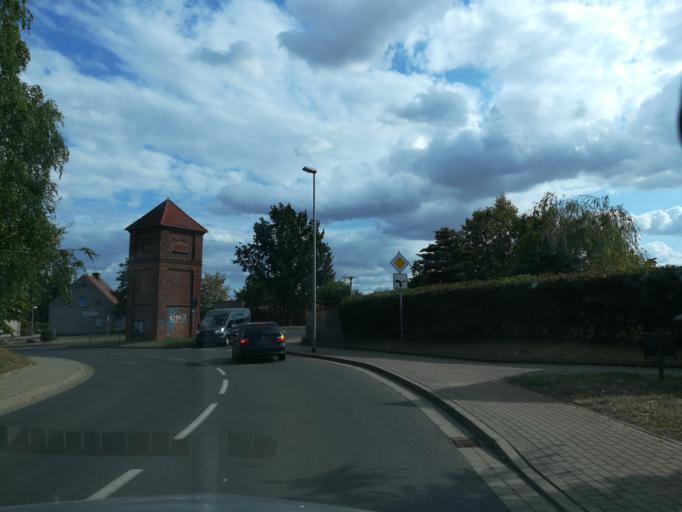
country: DE
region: Saxony-Anhalt
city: Niederndodeleben
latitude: 52.1401
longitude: 11.4962
